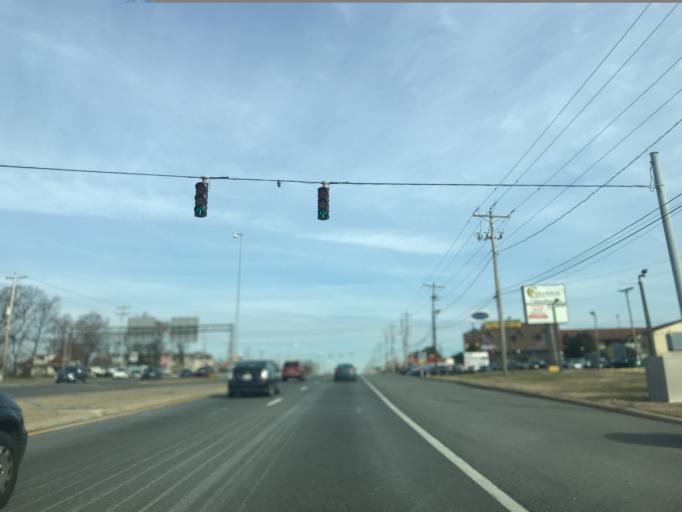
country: US
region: Delaware
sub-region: New Castle County
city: Wilmington Manor
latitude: 39.6533
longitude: -75.6176
